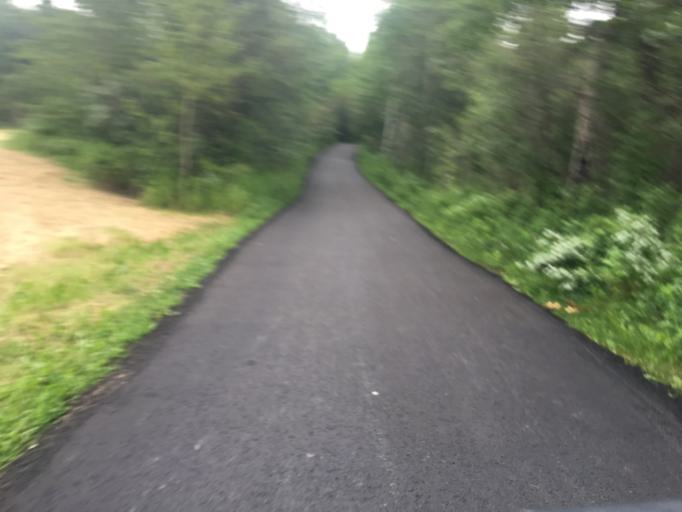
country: CA
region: Alberta
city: Grande Prairie
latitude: 55.1336
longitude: -118.7897
